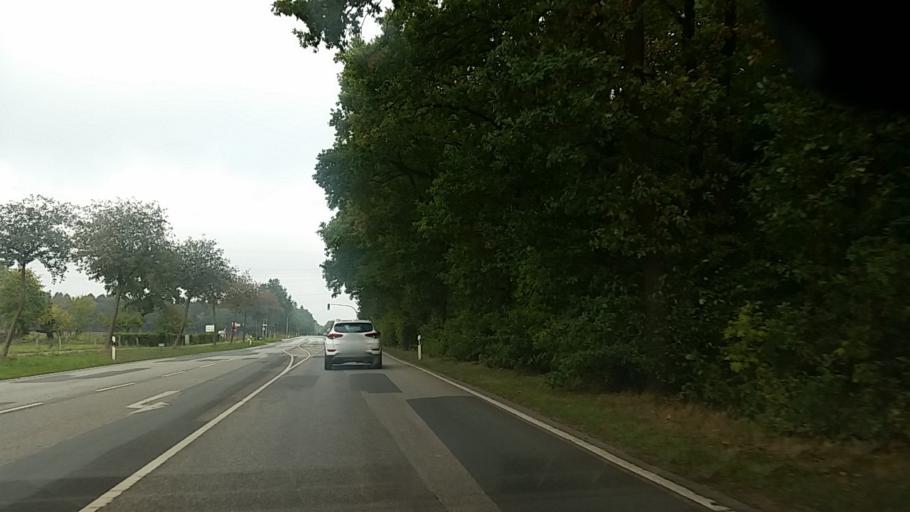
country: DE
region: Schleswig-Holstein
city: Henstedt-Ulzburg
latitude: 53.7552
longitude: 9.9872
